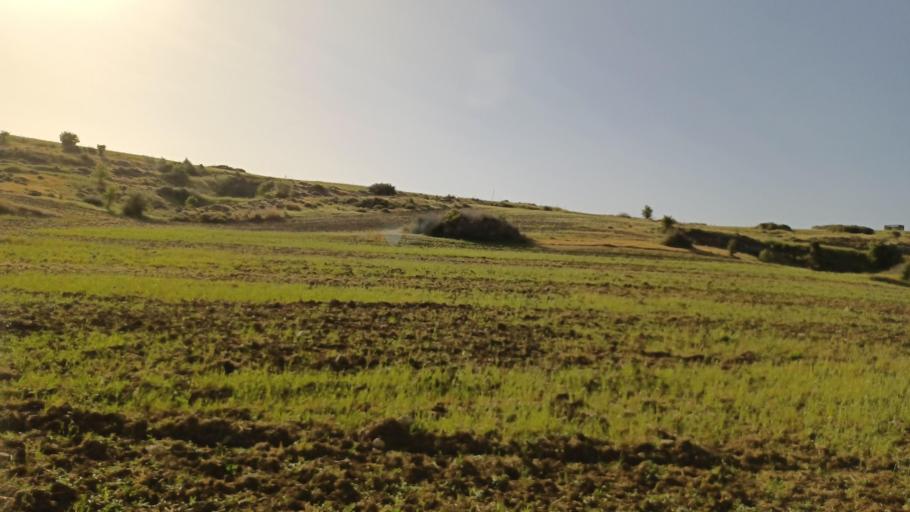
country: CY
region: Lefkosia
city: Astromeritis
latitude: 35.0817
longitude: 33.0292
